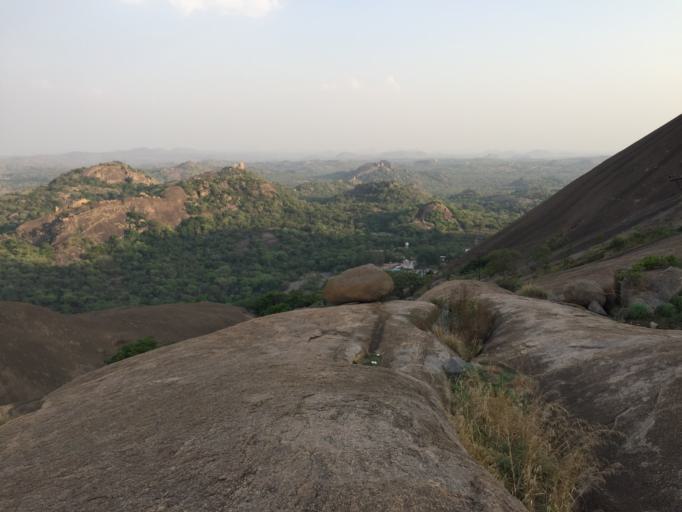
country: IN
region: Karnataka
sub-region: Ramanagara
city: Magadi
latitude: 12.9231
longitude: 77.2981
